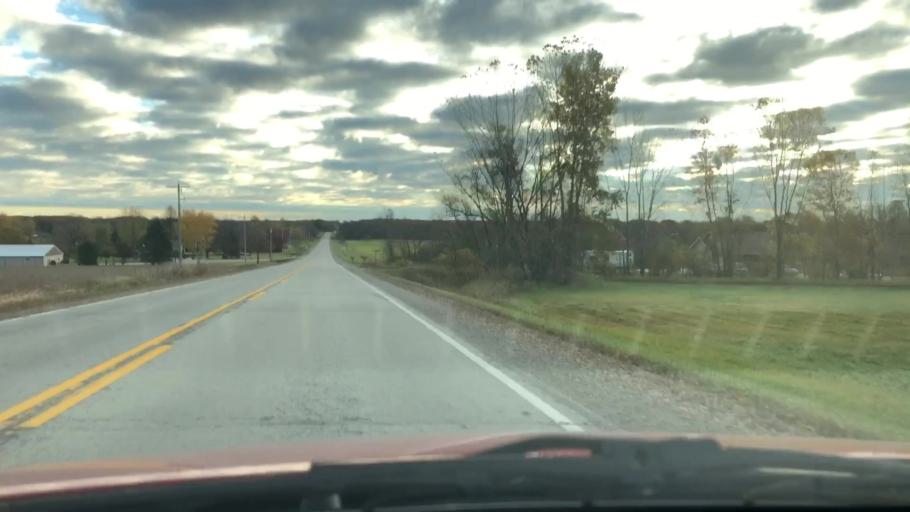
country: US
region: Wisconsin
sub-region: Brown County
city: Oneida
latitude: 44.4442
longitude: -88.2634
